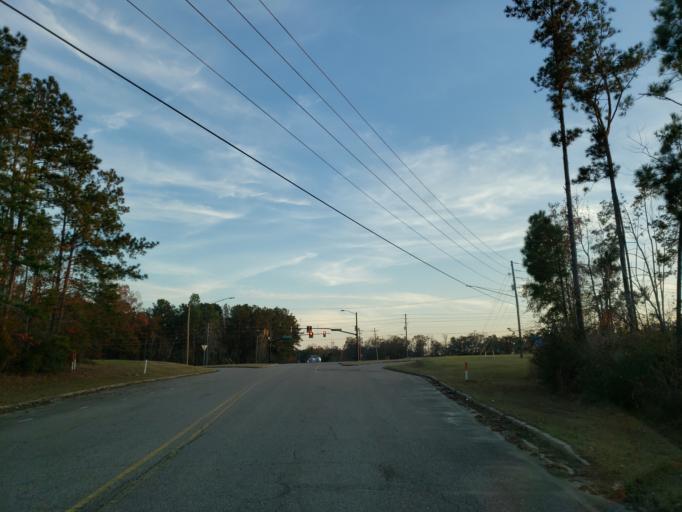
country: US
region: Mississippi
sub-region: Forrest County
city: Hattiesburg
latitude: 31.2914
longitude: -89.3137
